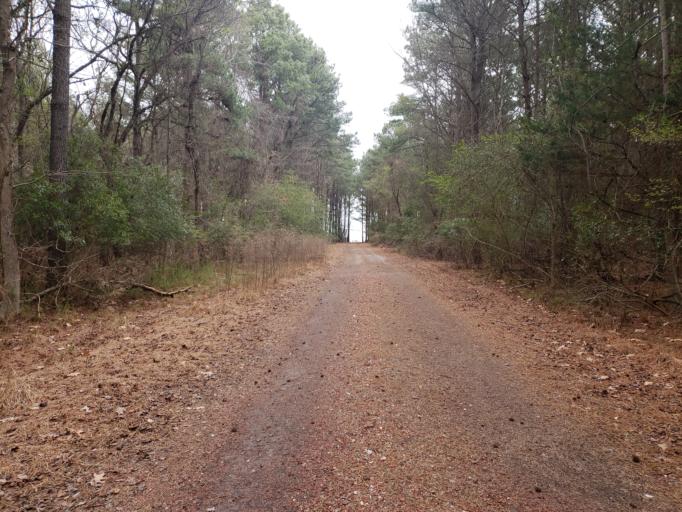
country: US
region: Virginia
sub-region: City of Newport News
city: Newport News
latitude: 36.9021
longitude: -76.4310
